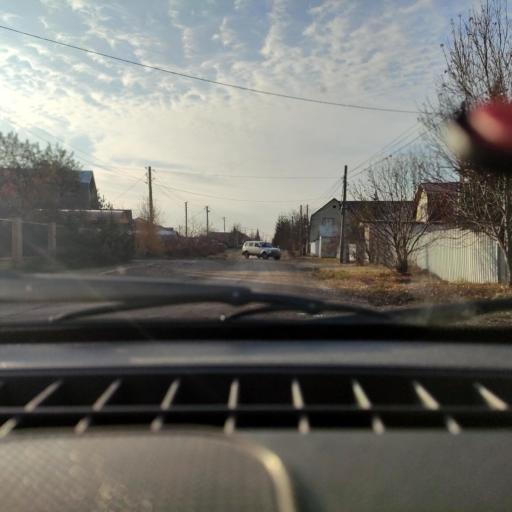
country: RU
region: Bashkortostan
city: Ufa
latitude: 54.6103
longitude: 55.9310
